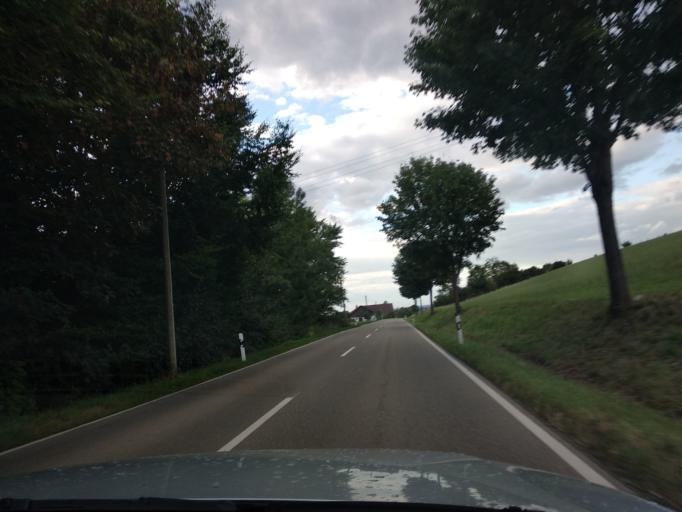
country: DE
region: Bavaria
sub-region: Swabia
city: Woringen
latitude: 47.9054
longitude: 10.2051
